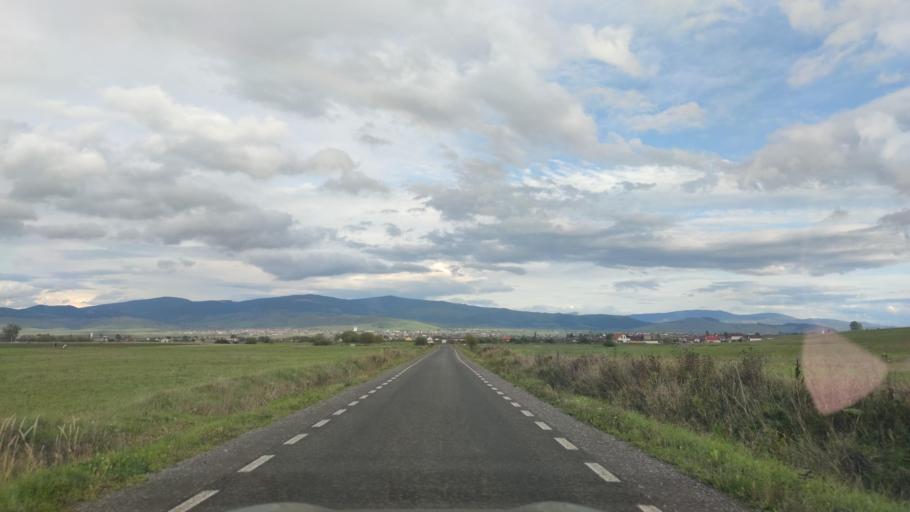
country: RO
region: Harghita
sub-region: Comuna Remetea
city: Remetea
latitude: 46.8056
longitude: 25.4283
